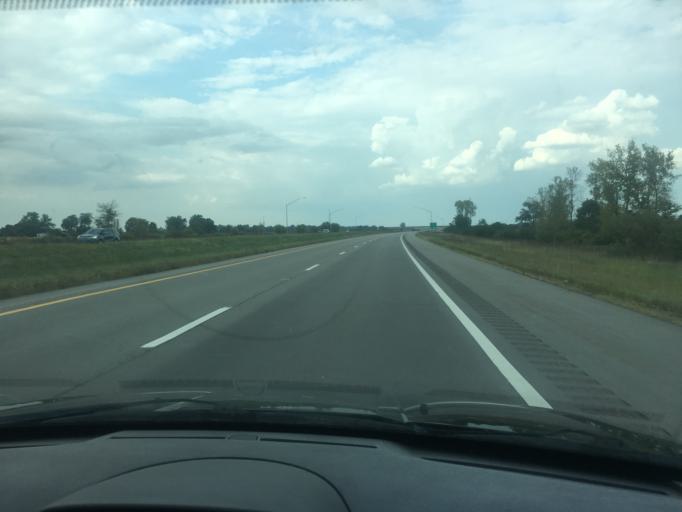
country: US
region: Ohio
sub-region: Clark County
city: Northridge
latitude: 40.0210
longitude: -83.8071
